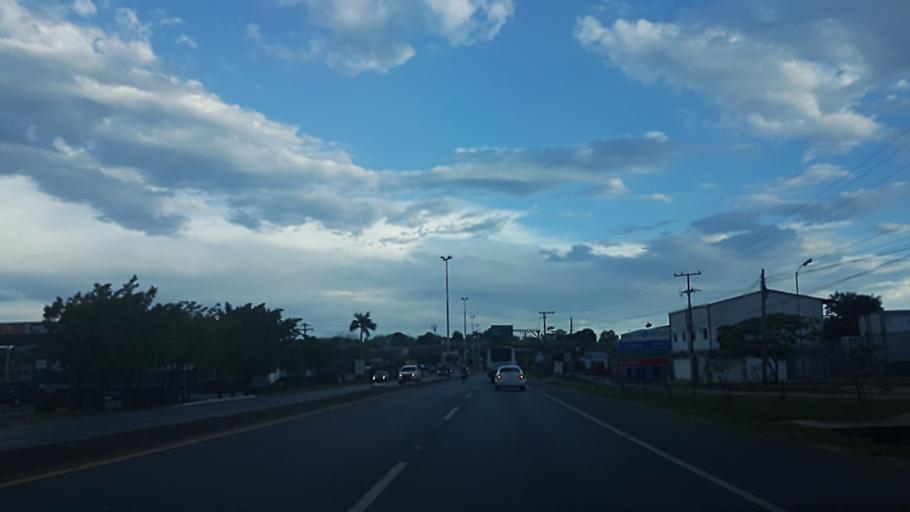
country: PY
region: Central
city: Colonia Mariano Roque Alonso
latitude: -25.2012
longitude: -57.5267
